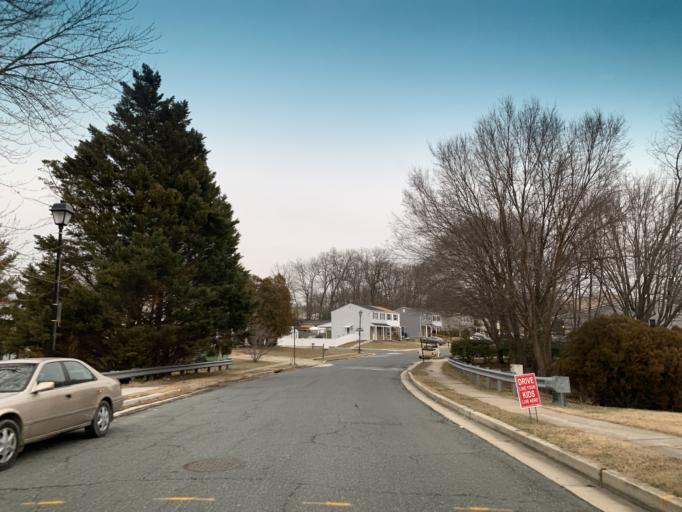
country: US
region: Maryland
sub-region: Baltimore County
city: Perry Hall
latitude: 39.3864
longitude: -76.4814
